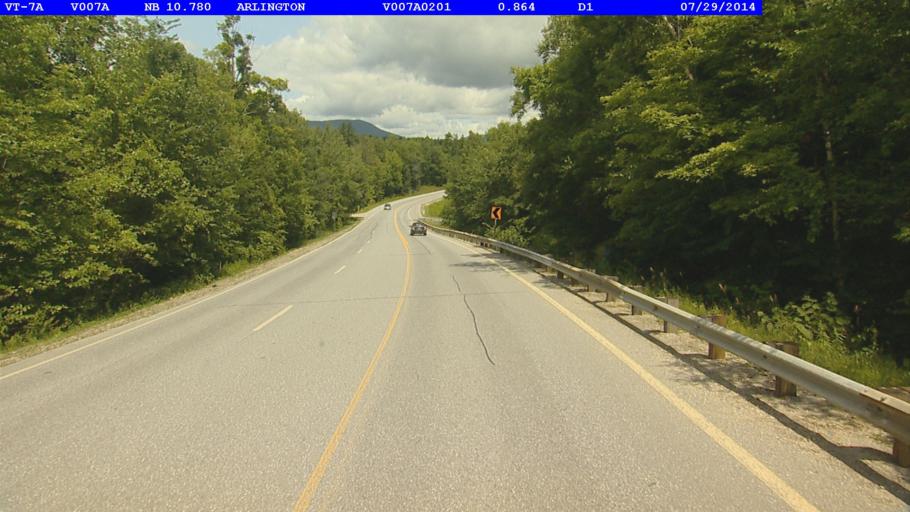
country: US
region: Vermont
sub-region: Bennington County
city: Arlington
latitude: 43.0363
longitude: -73.1763
